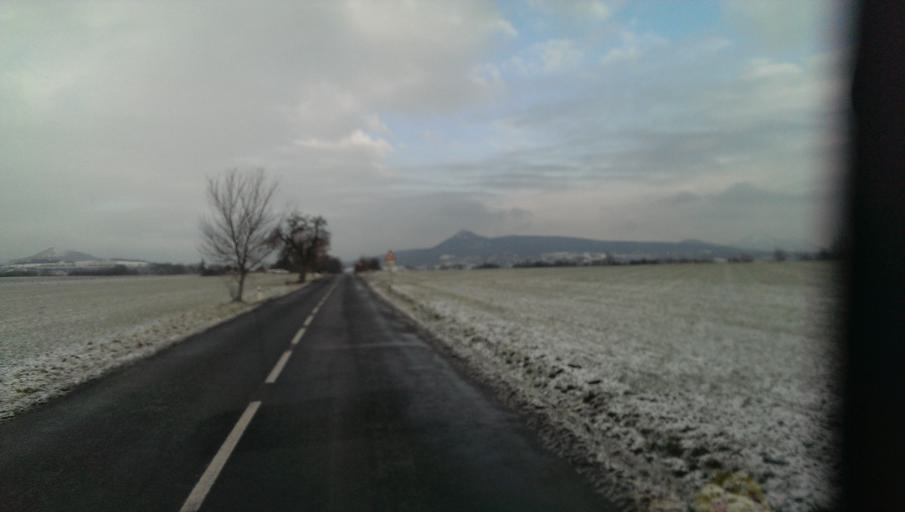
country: CZ
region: Ustecky
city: Trebenice
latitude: 50.4568
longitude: 13.9979
